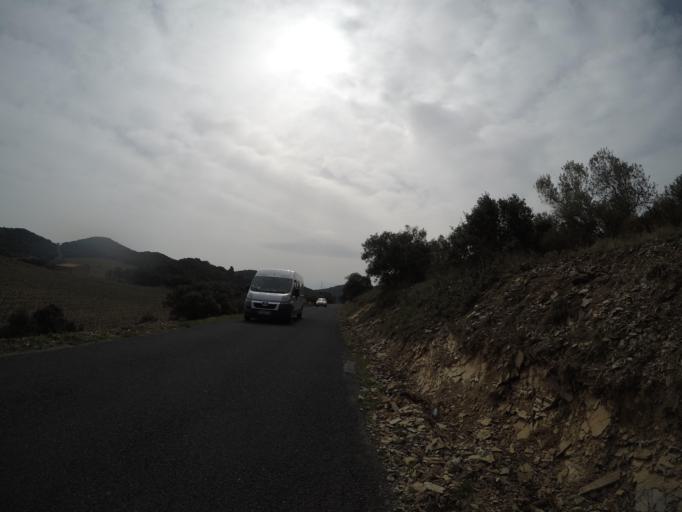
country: FR
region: Languedoc-Roussillon
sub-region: Departement des Pyrenees-Orientales
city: Corneilla-la-Riviere
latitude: 42.7391
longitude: 2.7297
